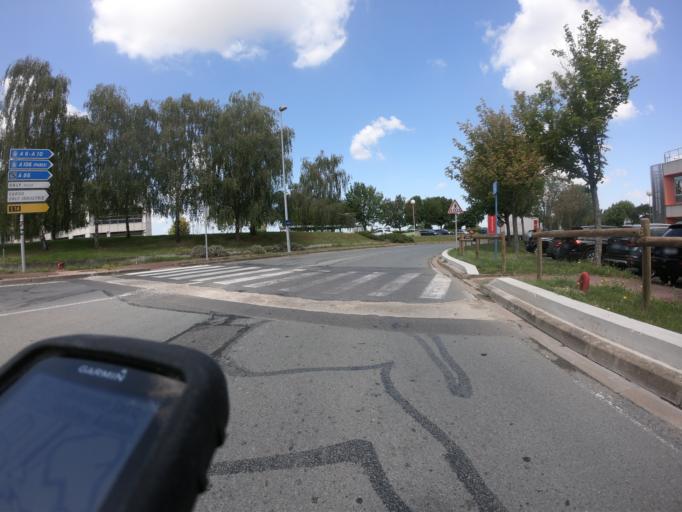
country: FR
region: Ile-de-France
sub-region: Departement du Val-de-Marne
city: Rungis
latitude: 48.7411
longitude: 2.3602
